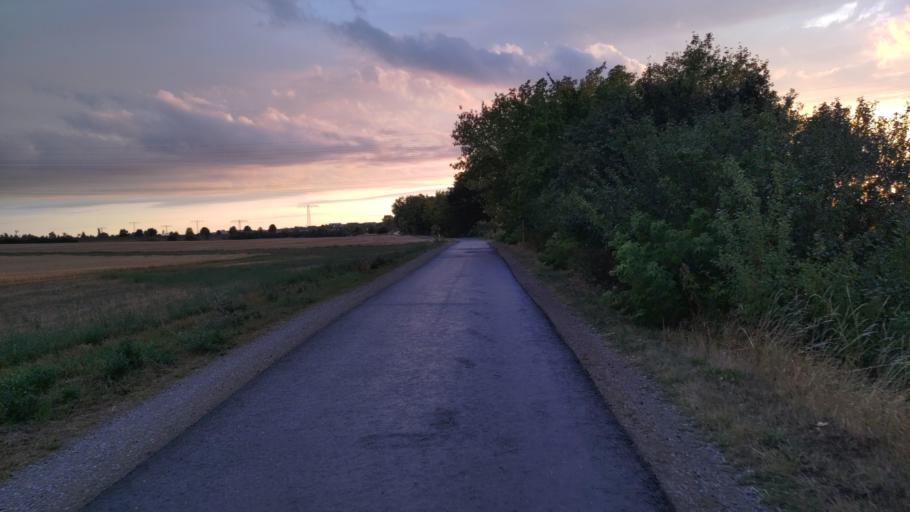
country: DE
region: Thuringia
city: Kleinmolsen
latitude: 50.9892
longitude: 11.0955
